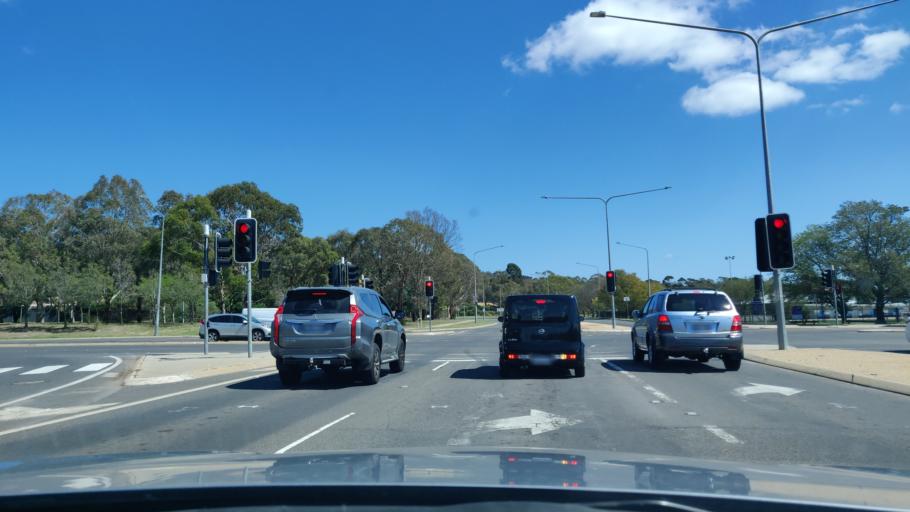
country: AU
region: Australian Capital Territory
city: Macarthur
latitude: -35.3644
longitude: 149.0928
